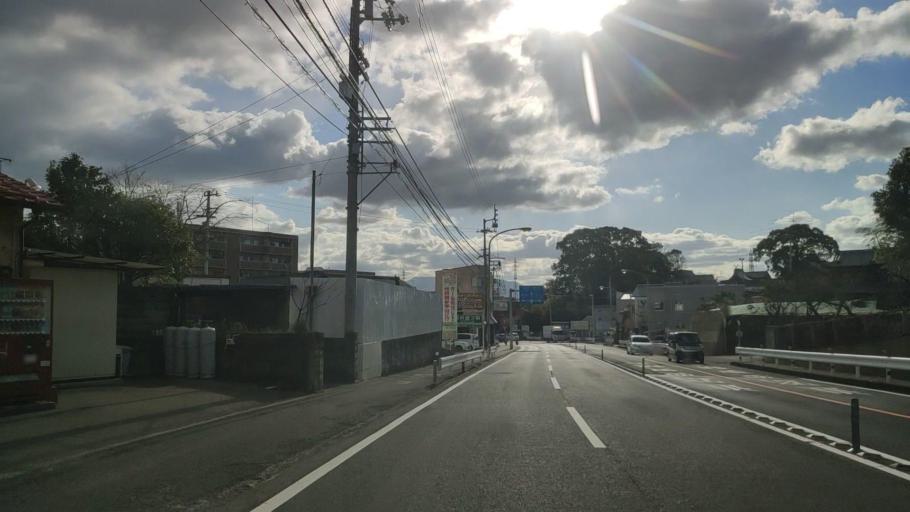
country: JP
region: Ehime
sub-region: Shikoku-chuo Shi
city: Matsuyama
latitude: 33.8570
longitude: 132.7419
